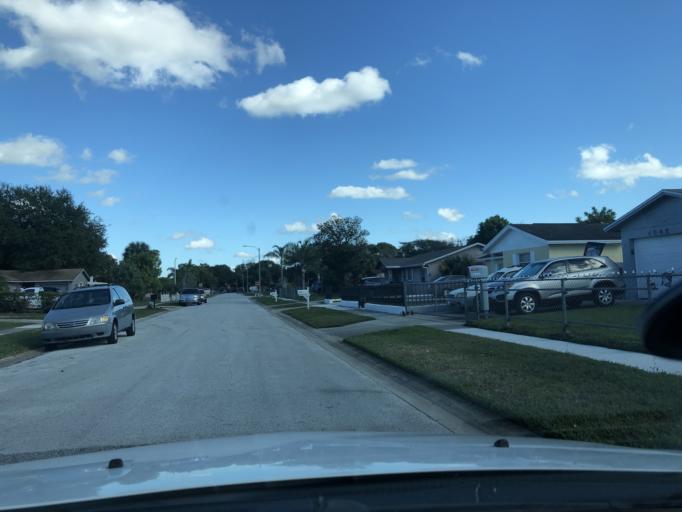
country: US
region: Florida
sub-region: Orange County
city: Oak Ridge
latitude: 28.4784
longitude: -81.4353
